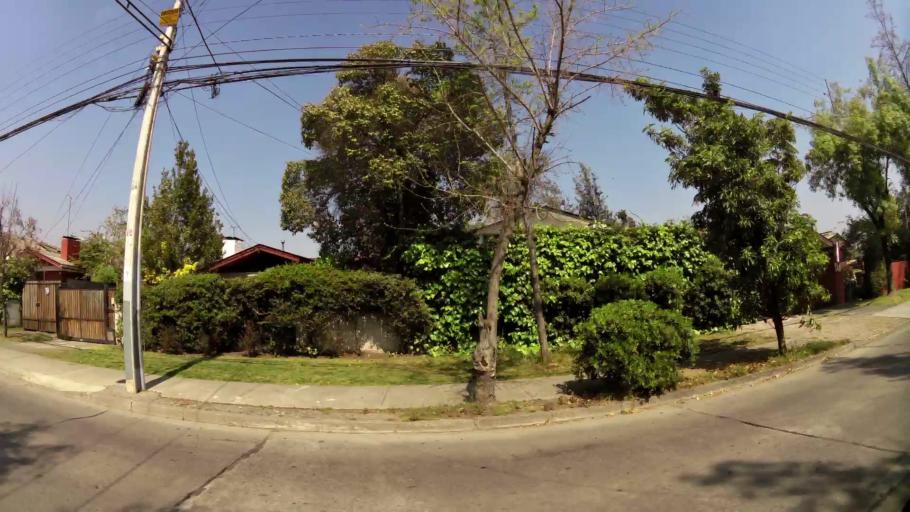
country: CL
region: Santiago Metropolitan
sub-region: Provincia de Santiago
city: Villa Presidente Frei, Nunoa, Santiago, Chile
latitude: -33.3853
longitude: -70.5676
